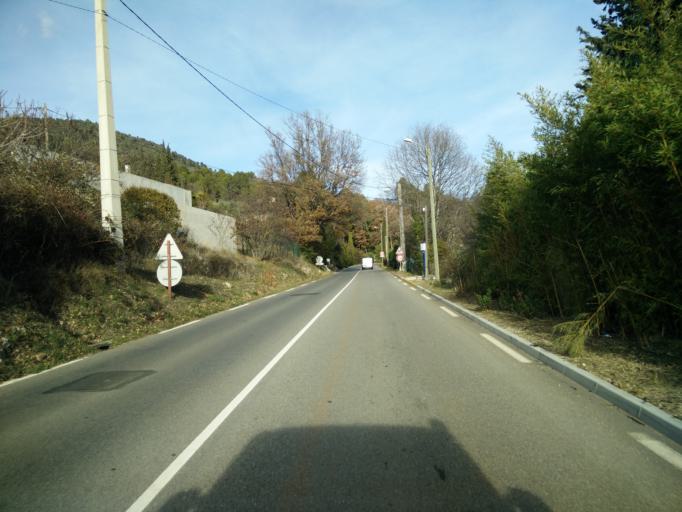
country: FR
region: Provence-Alpes-Cote d'Azur
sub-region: Departement des Alpes-Maritimes
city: Le Tignet
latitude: 43.6309
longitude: 6.8388
